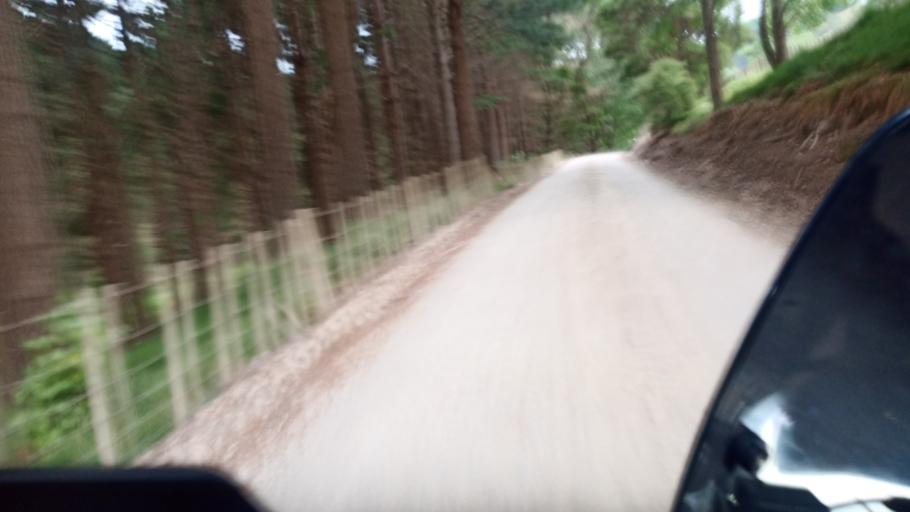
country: NZ
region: Gisborne
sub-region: Gisborne District
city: Gisborne
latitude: -38.4814
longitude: 177.9621
